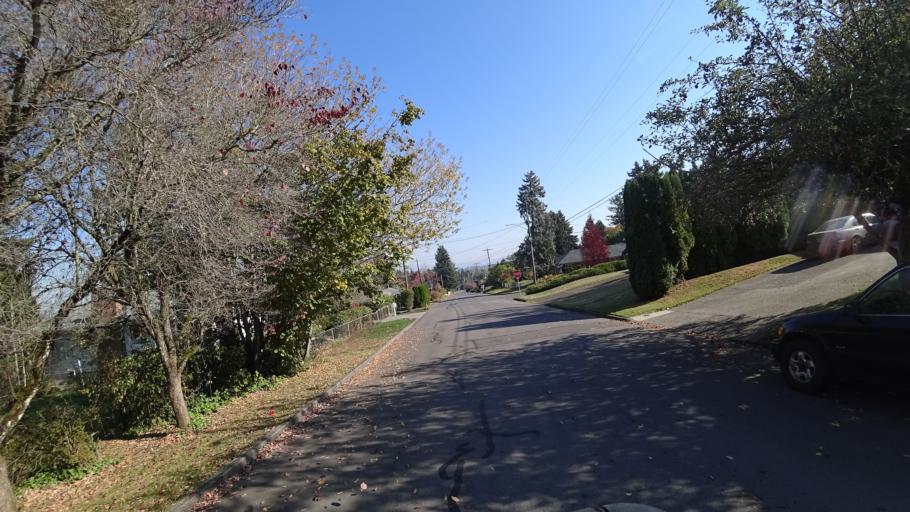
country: US
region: Oregon
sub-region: Multnomah County
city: Gresham
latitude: 45.5030
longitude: -122.4432
